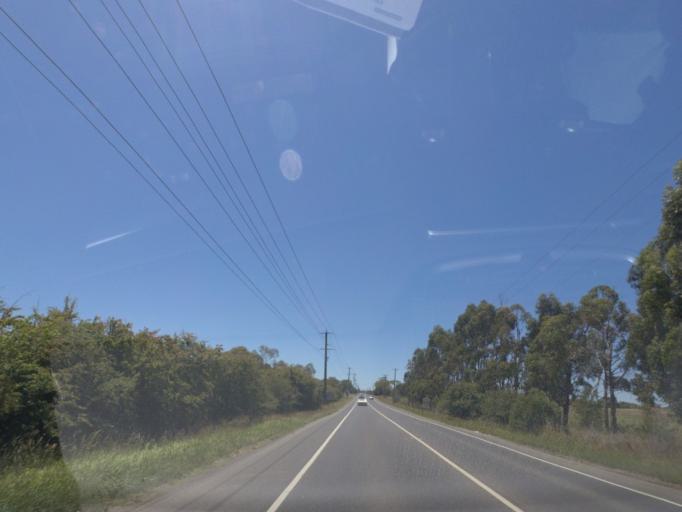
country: AU
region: Victoria
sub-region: Whittlesea
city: Epping
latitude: -37.6021
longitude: 145.0324
